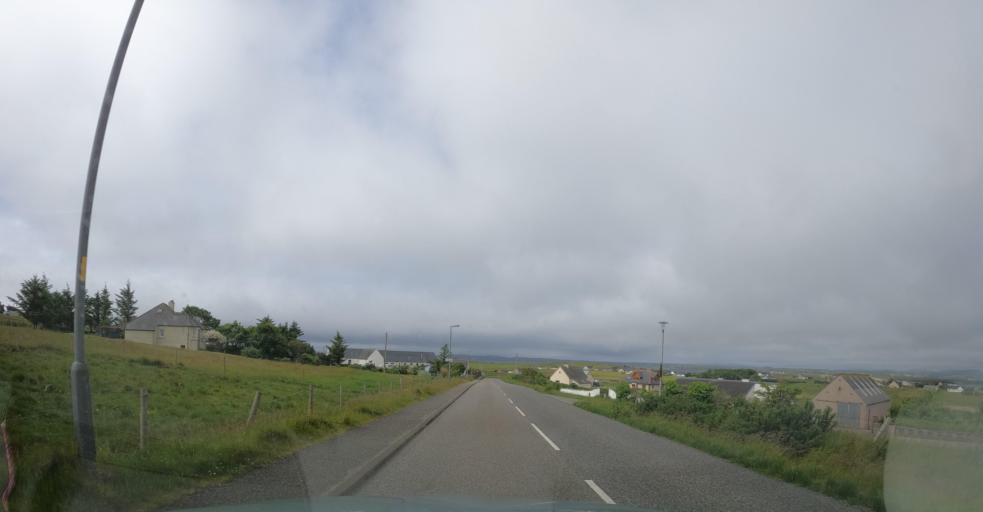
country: GB
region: Scotland
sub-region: Eilean Siar
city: Stornoway
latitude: 58.2063
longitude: -6.2689
